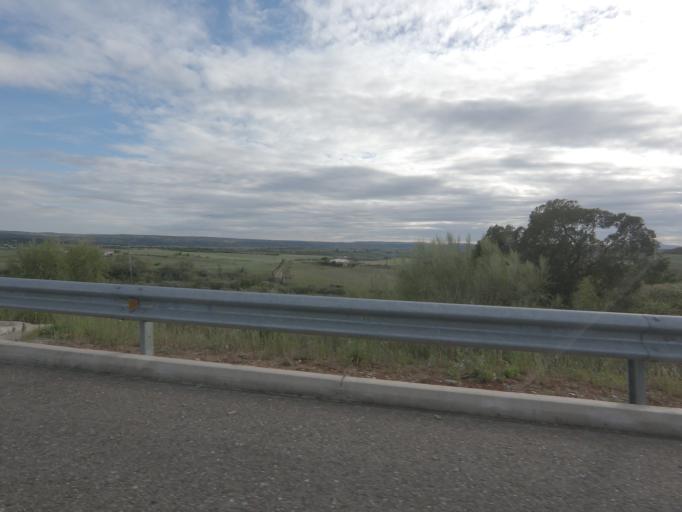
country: ES
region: Extremadura
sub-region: Provincia de Caceres
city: Coria
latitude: 40.0103
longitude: -6.5633
